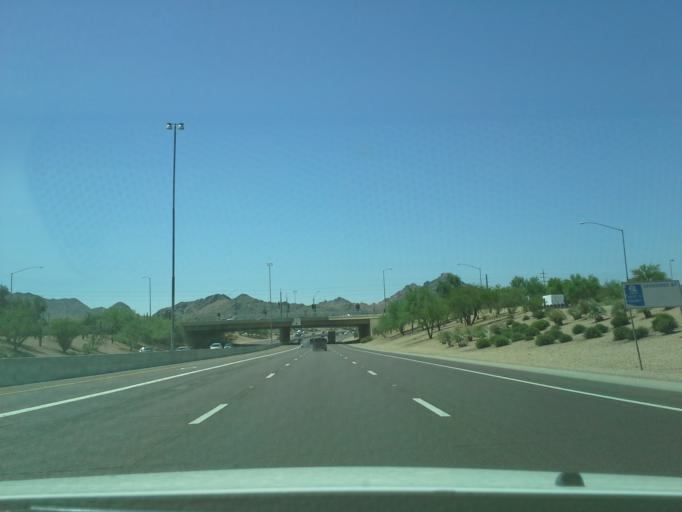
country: US
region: Arizona
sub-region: Maricopa County
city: Paradise Valley
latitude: 33.5847
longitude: -112.0099
